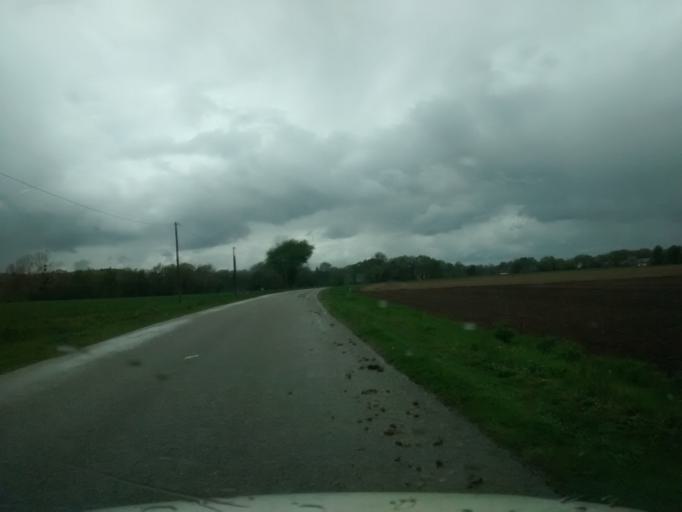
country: FR
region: Brittany
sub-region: Departement du Morbihan
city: Pleucadeuc
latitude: 47.7594
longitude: -2.3204
